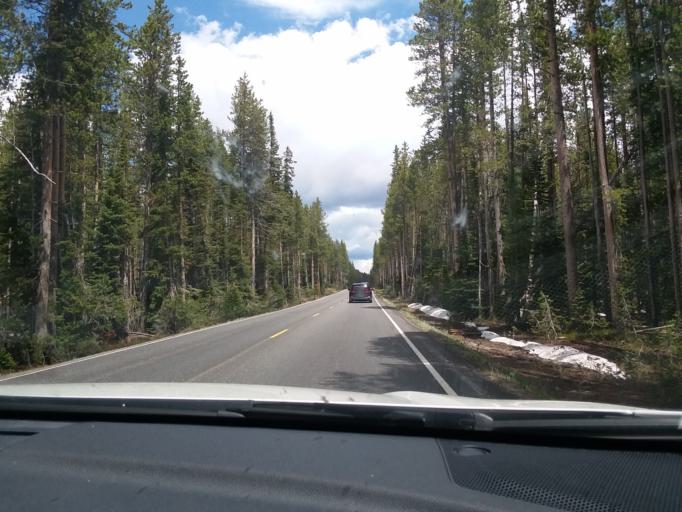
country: US
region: Idaho
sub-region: Teton County
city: Driggs
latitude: 44.1809
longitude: -110.6597
